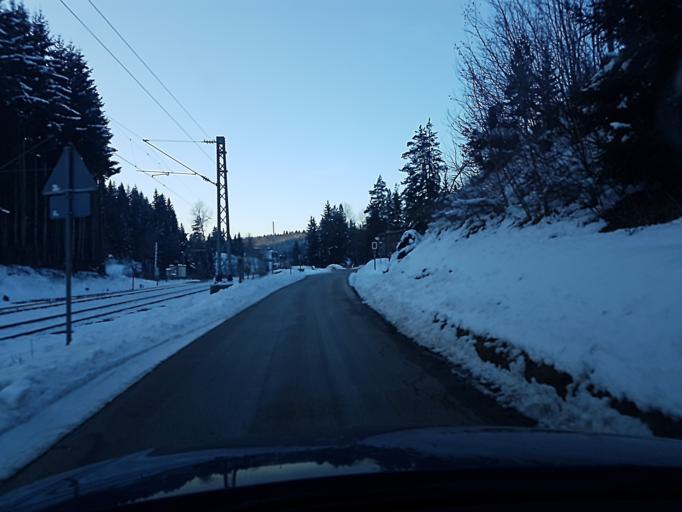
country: DE
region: Baden-Wuerttemberg
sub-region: Freiburg Region
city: Monchweiler
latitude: 48.0975
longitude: 8.3974
